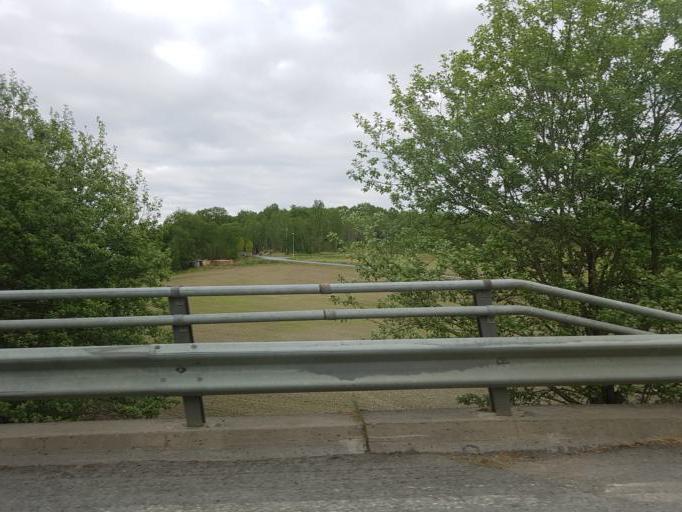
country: NO
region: Nord-Trondelag
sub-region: Levanger
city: Levanger
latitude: 63.7225
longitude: 11.2576
